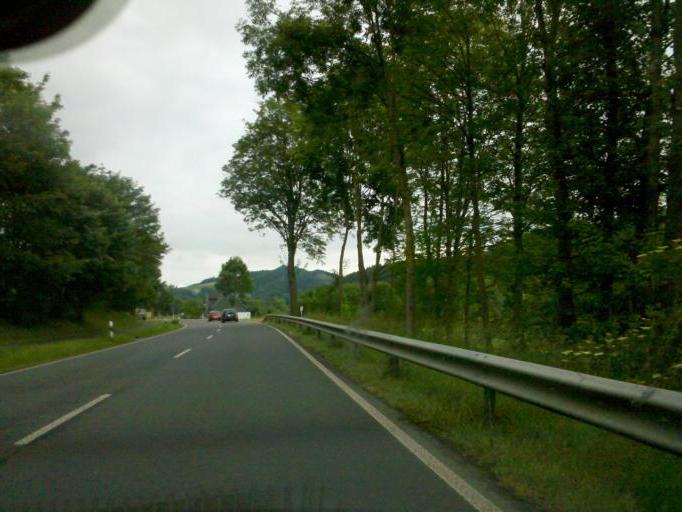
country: DE
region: North Rhine-Westphalia
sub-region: Regierungsbezirk Arnsberg
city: Lennestadt
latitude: 51.1562
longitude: 8.0848
